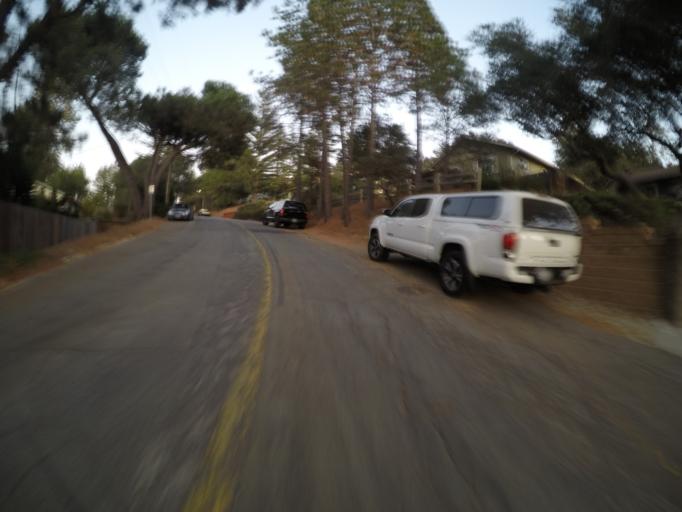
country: US
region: California
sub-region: Santa Cruz County
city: Mount Hermon
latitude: 37.0364
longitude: -122.0395
